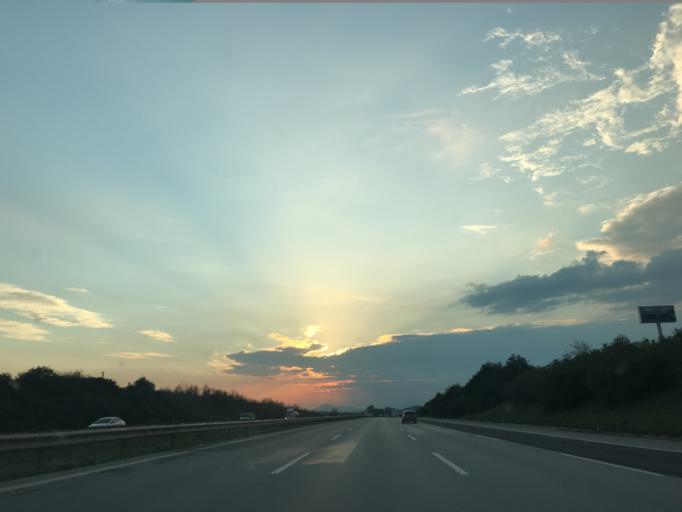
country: TR
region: Mersin
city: Yenice
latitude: 37.0219
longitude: 35.0410
